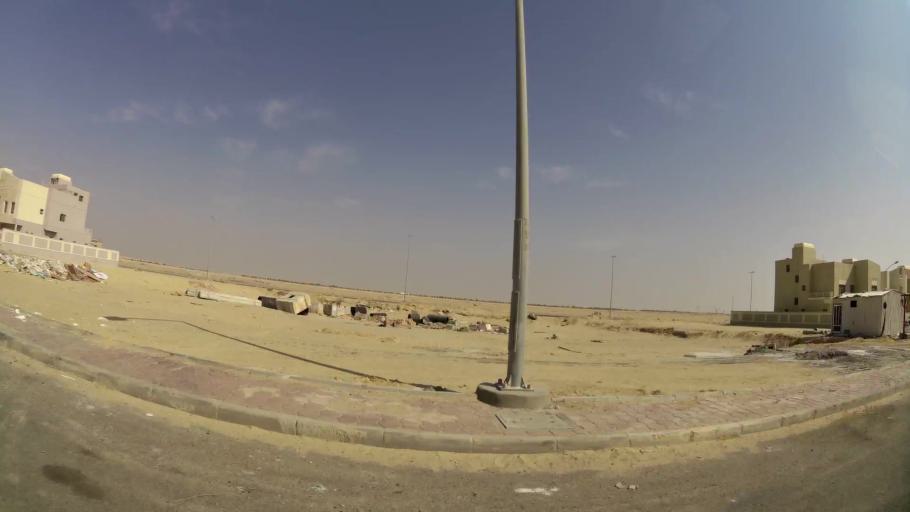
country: KW
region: Al Ahmadi
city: Al Wafrah
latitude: 28.8062
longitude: 48.0658
